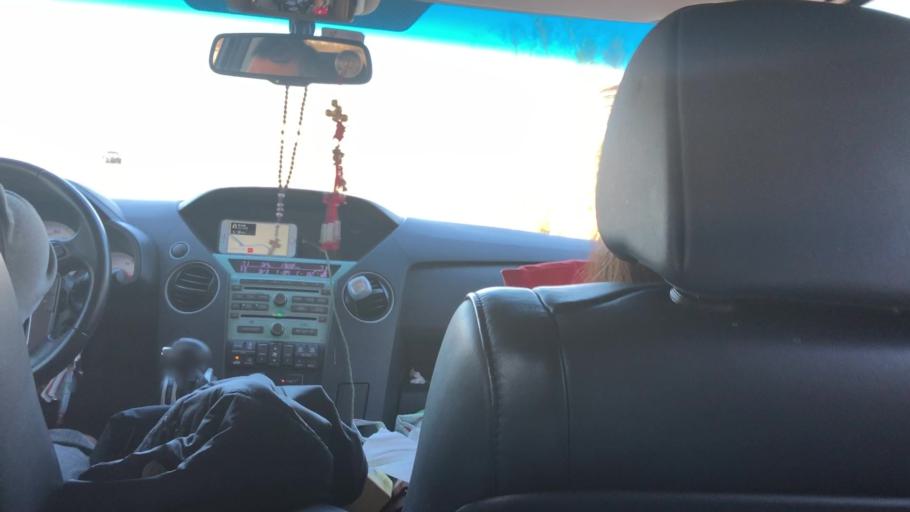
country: US
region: Louisiana
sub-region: Saint John the Baptist Parish
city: Montegut
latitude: 30.1068
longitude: -90.4938
